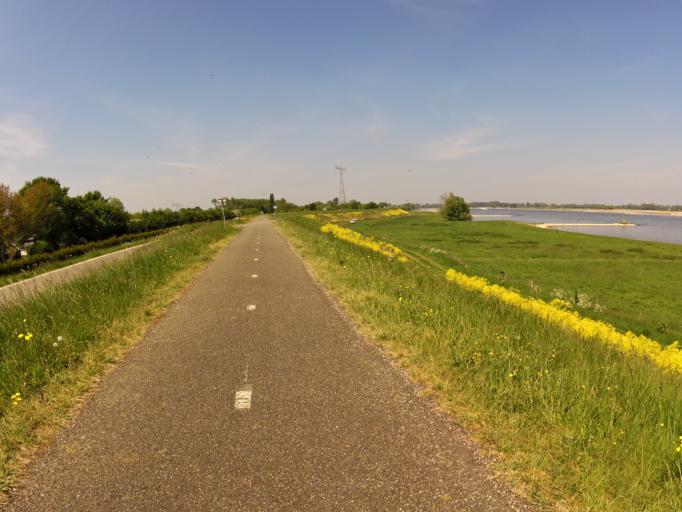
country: NL
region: Gelderland
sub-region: Gemeente Maasdriel
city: Heerewaarden
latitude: 51.8046
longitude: 5.3360
